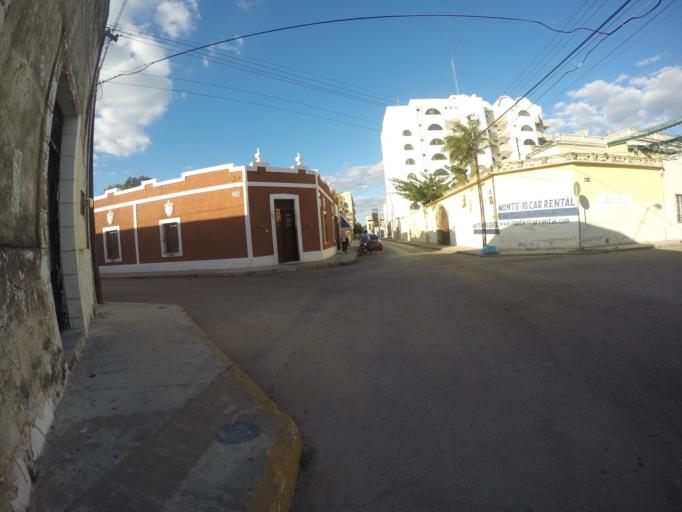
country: MX
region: Yucatan
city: Merida
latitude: 20.9789
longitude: -89.6196
